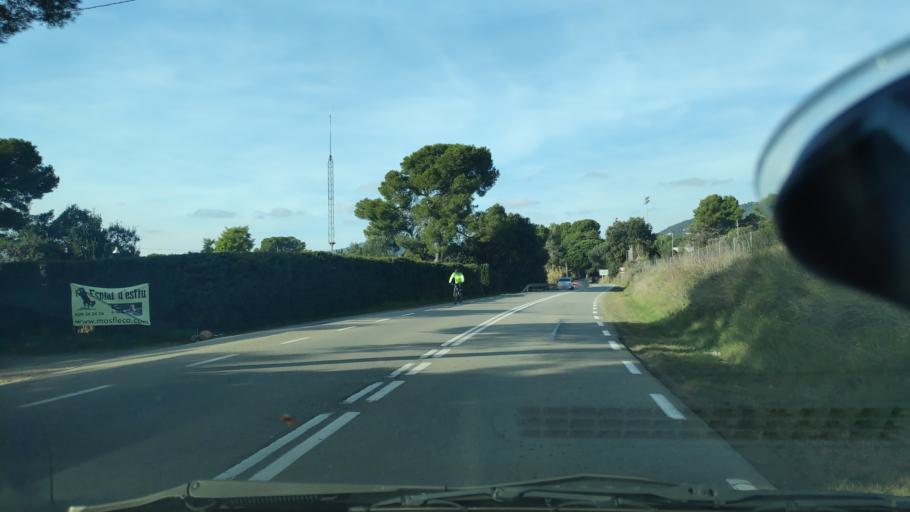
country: ES
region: Catalonia
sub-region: Provincia de Barcelona
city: Matadepera
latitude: 41.5924
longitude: 2.0420
